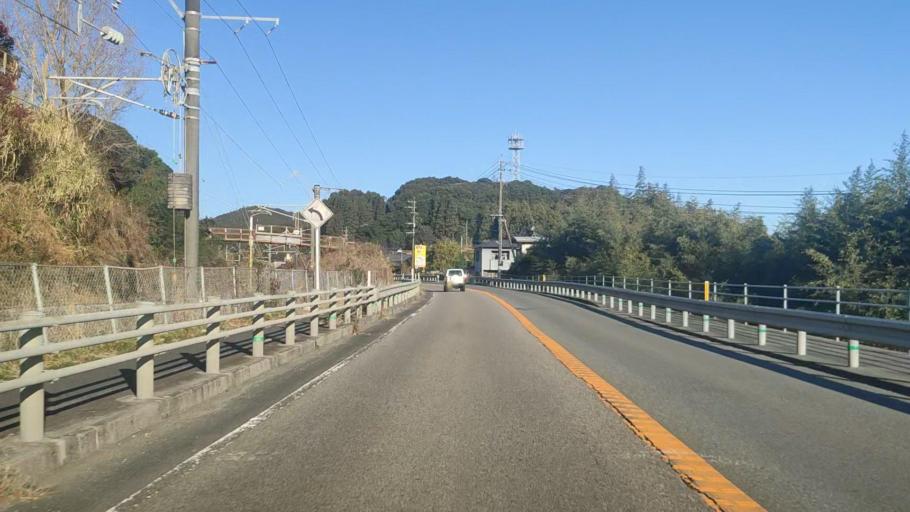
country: JP
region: Miyazaki
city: Nobeoka
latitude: 32.3752
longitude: 131.6302
